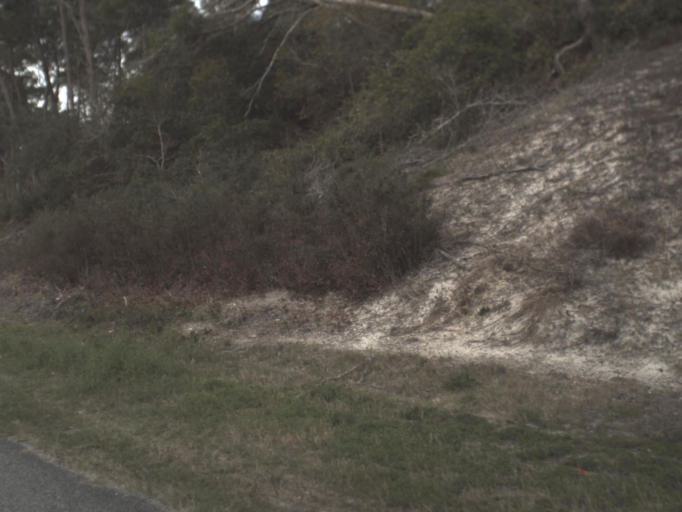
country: US
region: Florida
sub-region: Franklin County
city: Carrabelle
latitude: 29.7936
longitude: -84.7504
